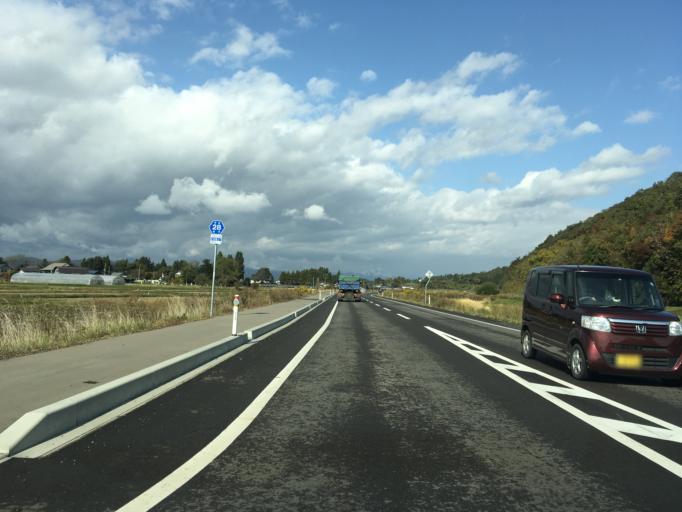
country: JP
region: Iwate
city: Hanamaki
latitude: 39.3678
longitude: 141.1487
